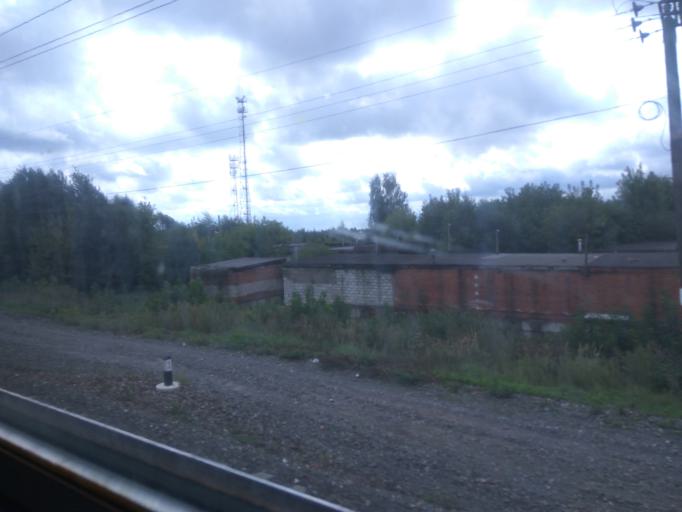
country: RU
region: Moskovskaya
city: Beloozerskiy
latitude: 55.4492
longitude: 38.4841
